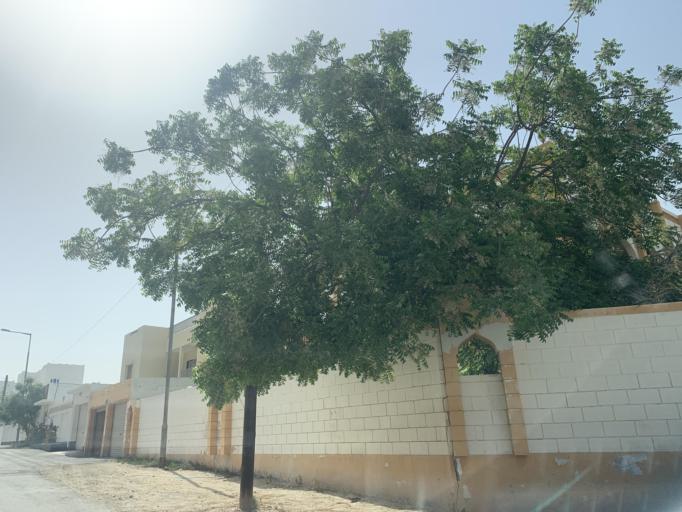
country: BH
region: Northern
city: Madinat `Isa
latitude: 26.1527
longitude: 50.5320
